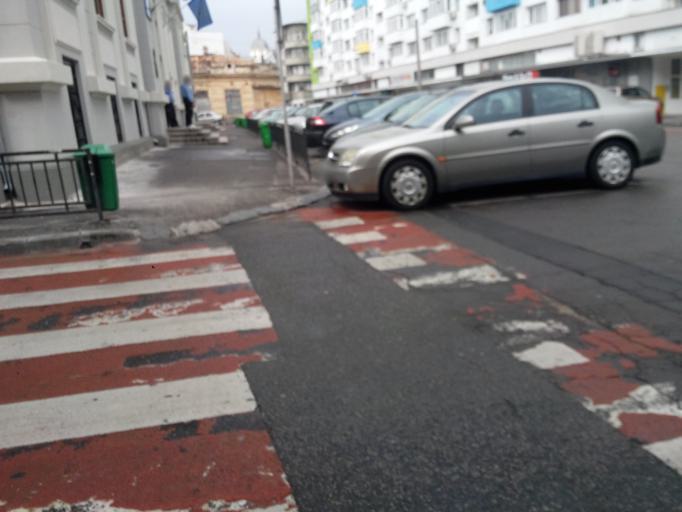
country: RO
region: Bucuresti
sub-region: Municipiul Bucuresti
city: Bucuresti
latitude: 44.4211
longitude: 26.1024
